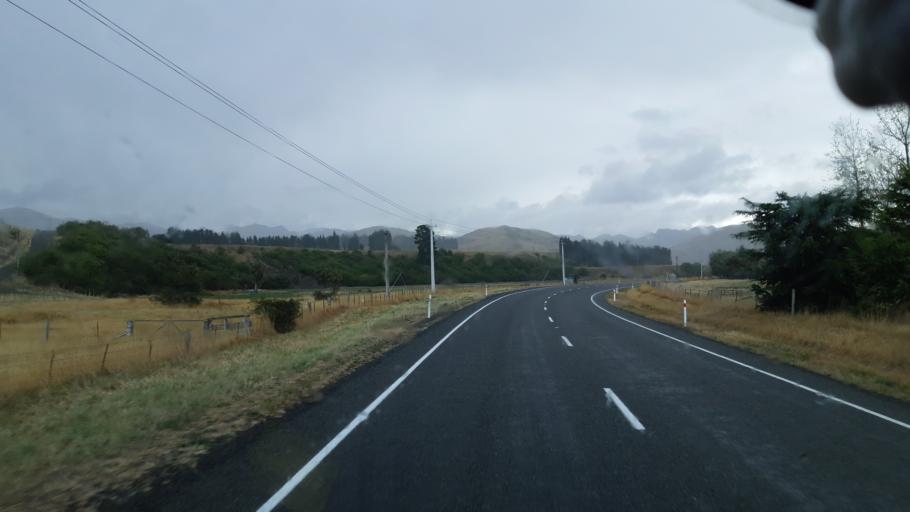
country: NZ
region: Canterbury
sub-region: Hurunui District
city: Amberley
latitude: -42.6967
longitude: 172.8017
